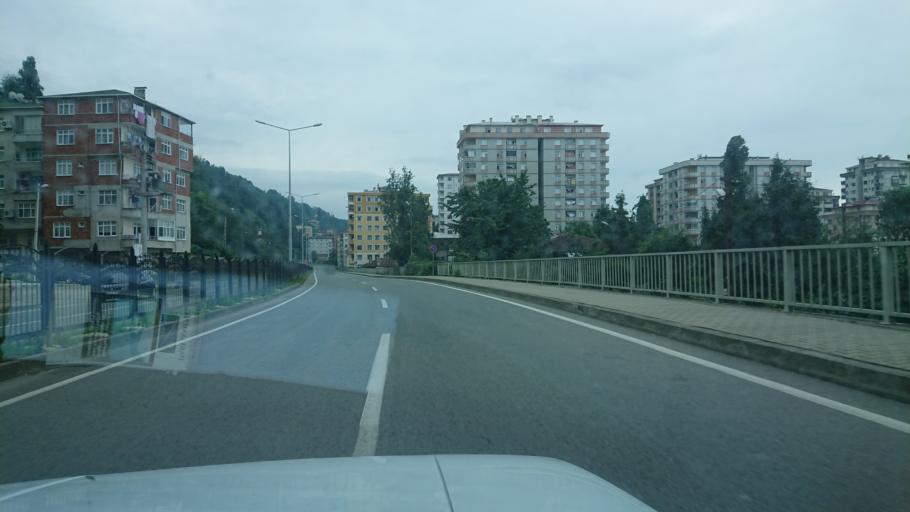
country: TR
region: Rize
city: Rize
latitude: 41.0319
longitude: 40.5601
